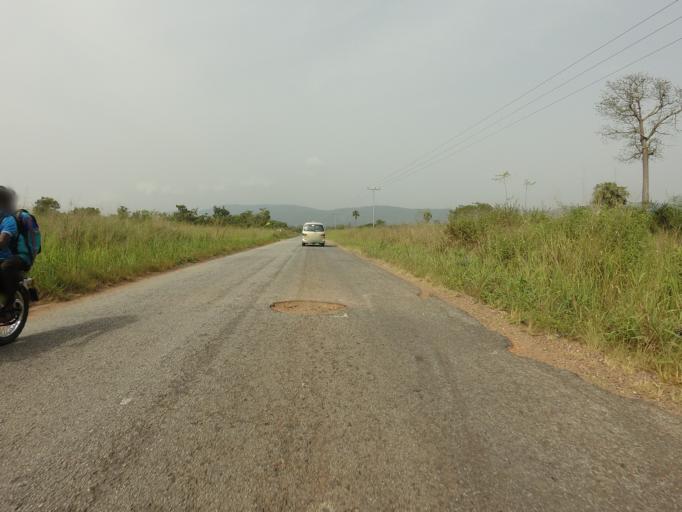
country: GH
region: Volta
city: Ho
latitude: 6.5737
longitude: 0.3486
